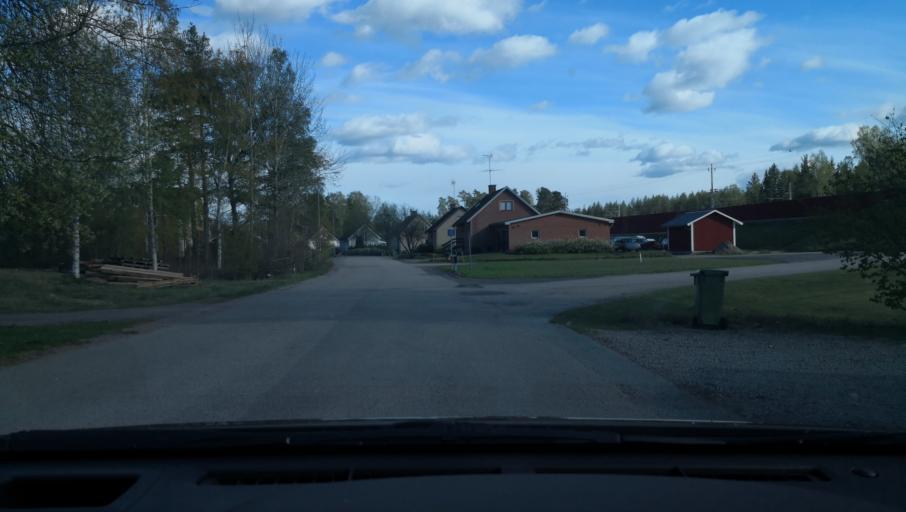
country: SE
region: OErebro
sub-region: Askersunds Kommun
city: Asbro
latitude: 58.9204
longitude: 15.0545
